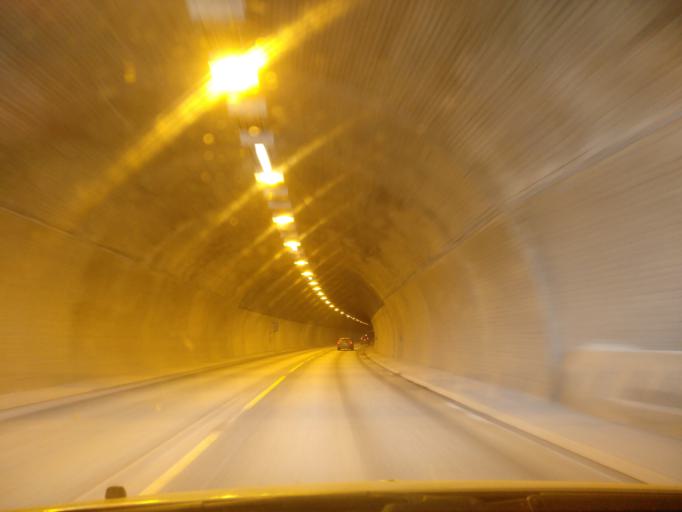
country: NO
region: Hordaland
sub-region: Etne
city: Etne
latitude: 59.7221
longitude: 6.1154
